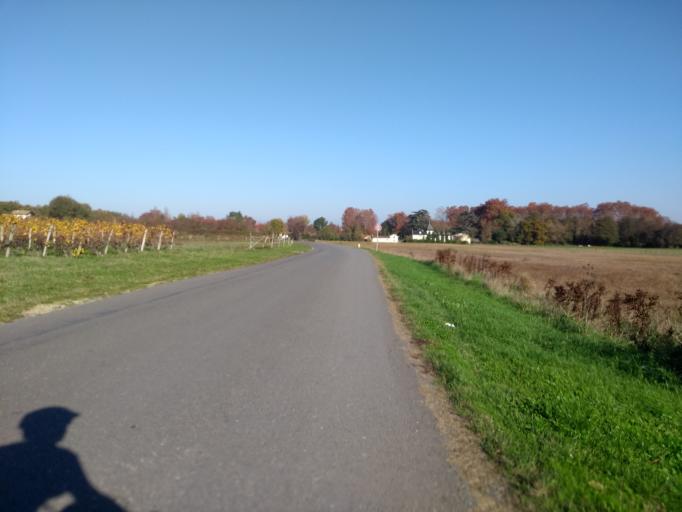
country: FR
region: Aquitaine
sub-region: Departement de la Gironde
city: Martillac
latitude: 44.6939
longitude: -0.5163
